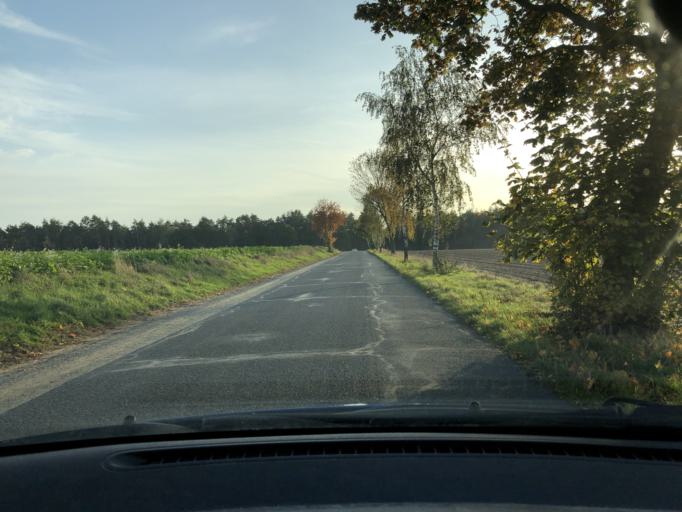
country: DE
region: Lower Saxony
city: Hitzacker
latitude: 53.1330
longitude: 11.0282
